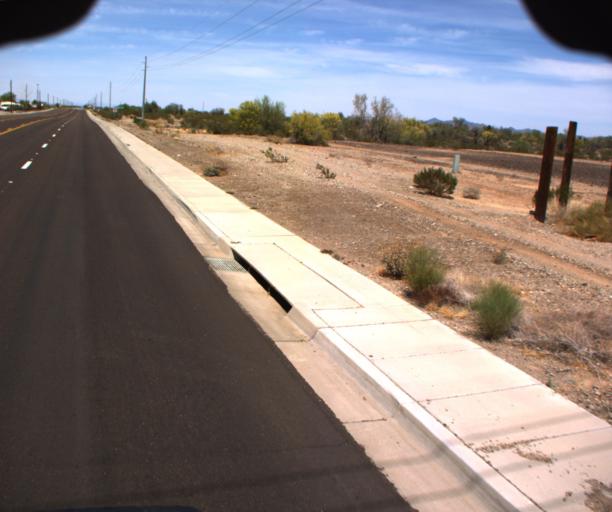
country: US
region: Arizona
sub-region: La Paz County
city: Quartzsite
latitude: 33.6821
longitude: -114.2170
